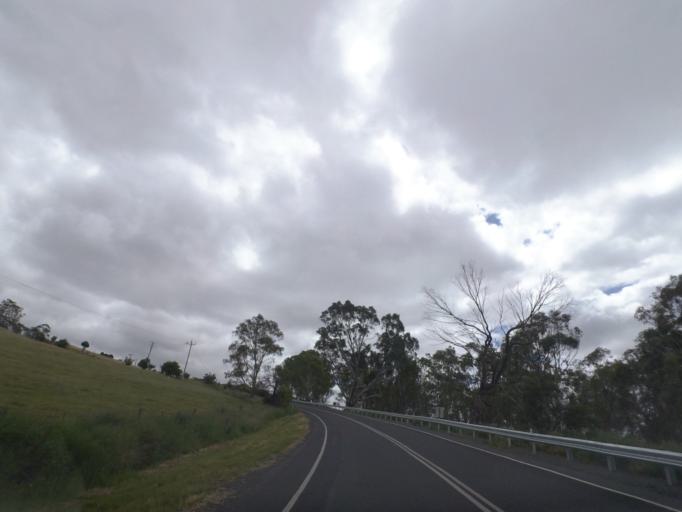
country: AU
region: Victoria
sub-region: Whittlesea
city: Whittlesea
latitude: -37.1900
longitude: 145.0390
